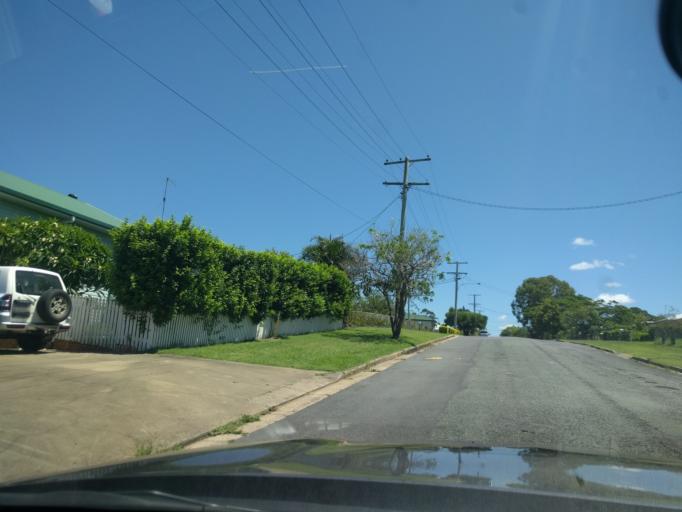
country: AU
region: Queensland
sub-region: Logan
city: Cedar Vale
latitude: -27.9914
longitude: 153.0063
